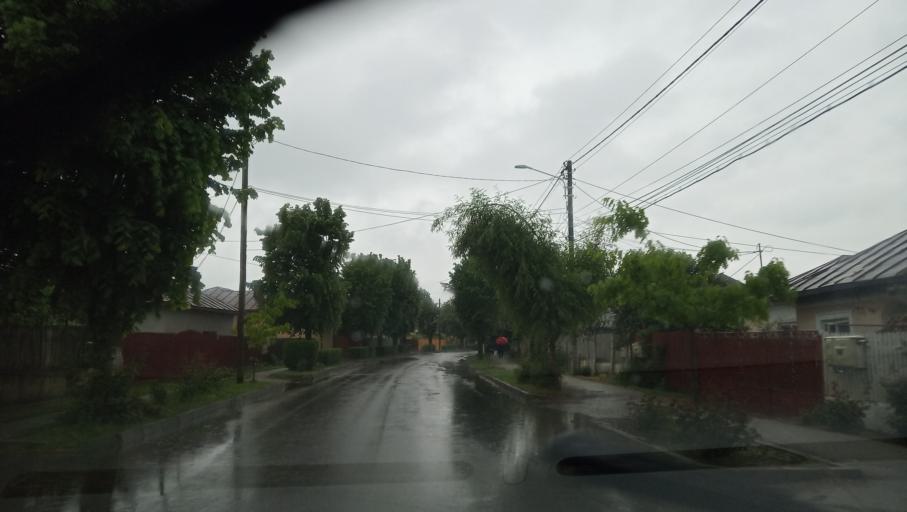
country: RO
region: Dambovita
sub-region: Oras Gaesti
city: Gaesti
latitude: 44.7158
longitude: 25.3163
